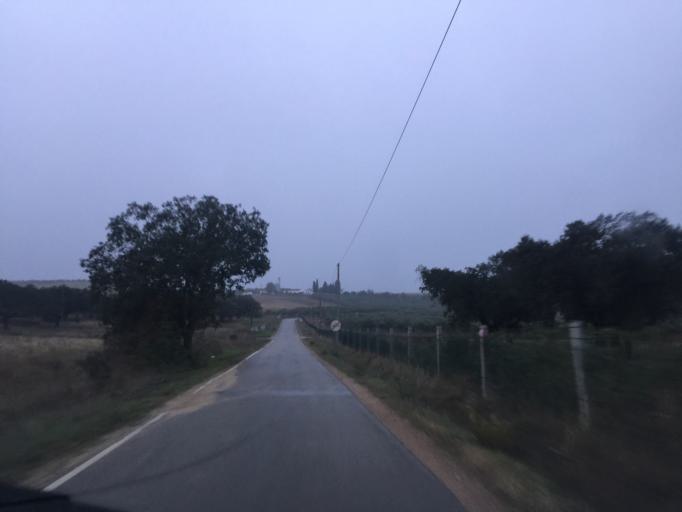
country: PT
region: Portalegre
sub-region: Avis
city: Avis
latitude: 39.0477
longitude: -7.9062
